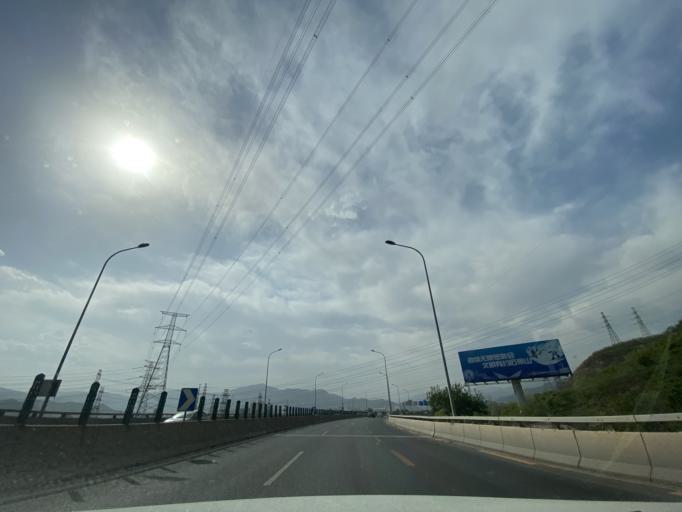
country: CN
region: Beijing
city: Guangning
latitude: 39.9284
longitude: 116.1296
